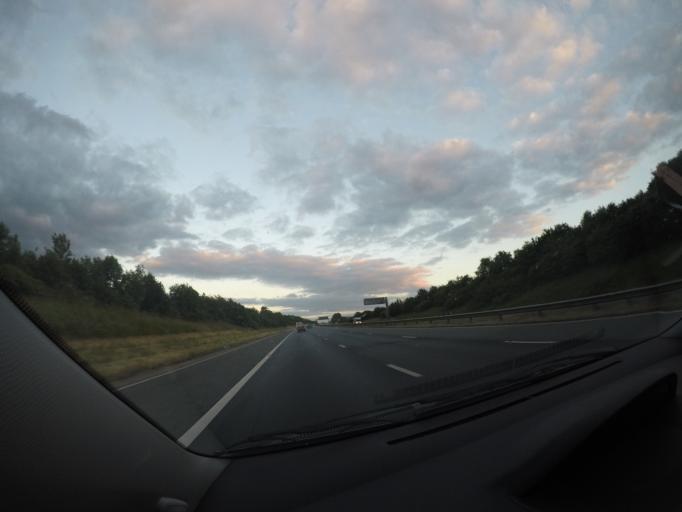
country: GB
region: England
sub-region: North Yorkshire
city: Boroughbridge
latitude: 54.0810
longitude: -1.3968
